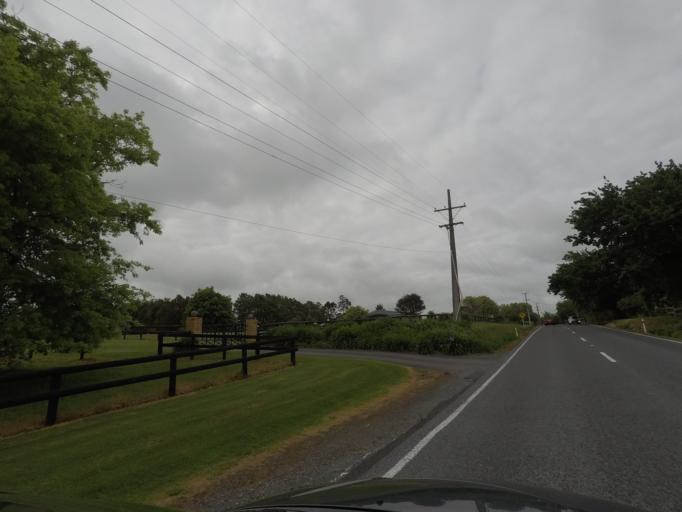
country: NZ
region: Auckland
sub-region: Auckland
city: Rosebank
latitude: -36.7903
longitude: 174.5752
